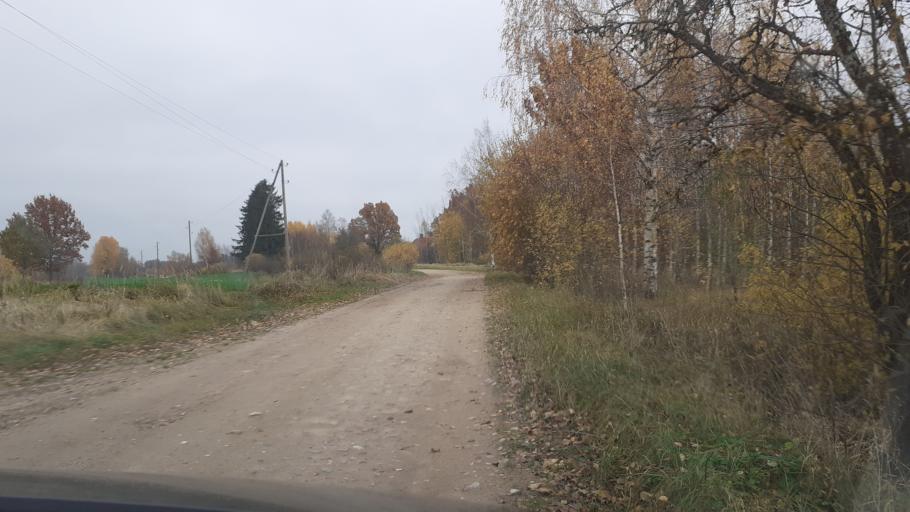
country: LV
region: Saldus Rajons
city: Saldus
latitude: 56.8637
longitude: 22.3199
